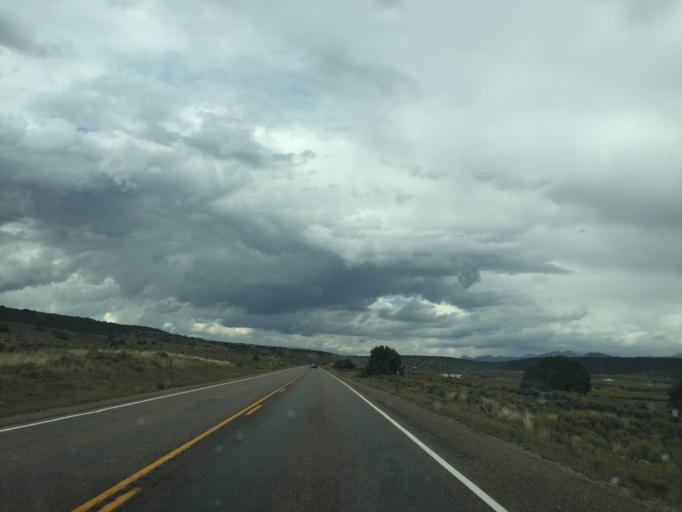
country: US
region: Utah
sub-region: Garfield County
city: Panguitch
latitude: 37.7347
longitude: -112.3797
